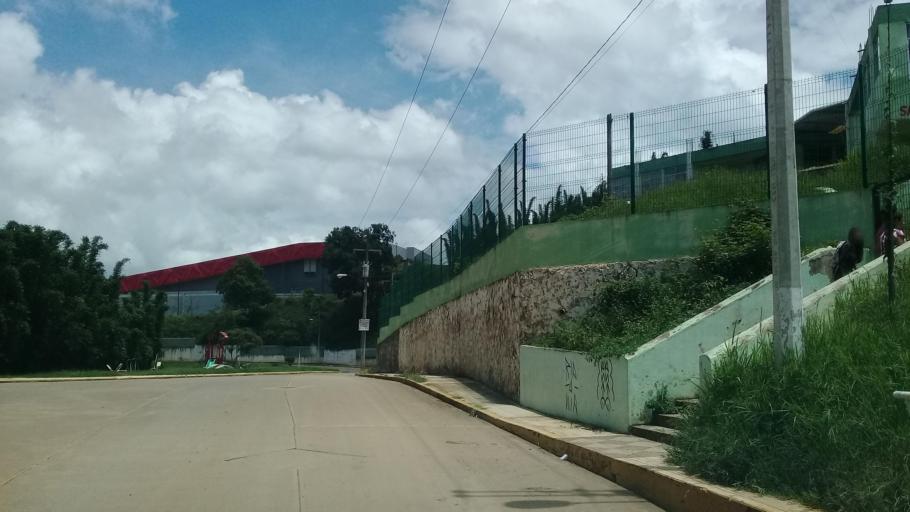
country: MX
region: Veracruz
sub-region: Xalapa
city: Fraccionamiento las Fuentes
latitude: 19.5003
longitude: -96.8840
